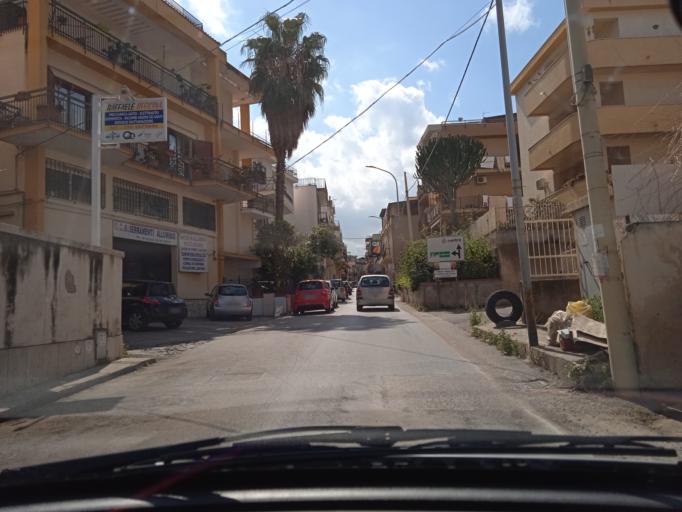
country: IT
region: Sicily
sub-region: Palermo
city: Casteldaccia
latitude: 38.0572
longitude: 13.5333
